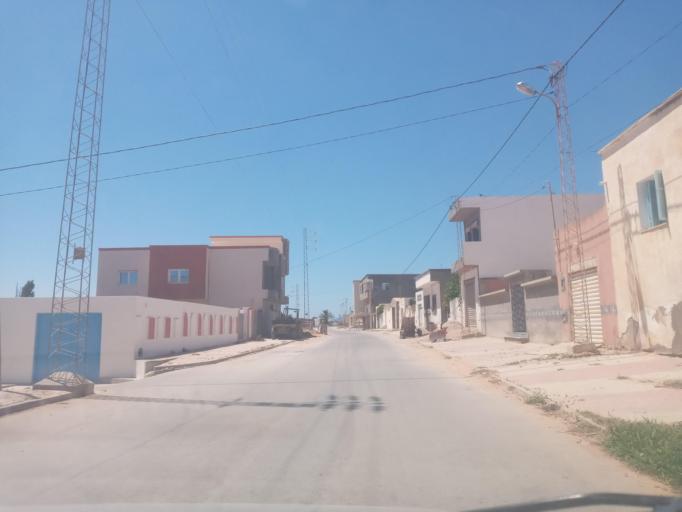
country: TN
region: Nabul
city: El Haouaria
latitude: 37.0503
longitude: 11.0018
